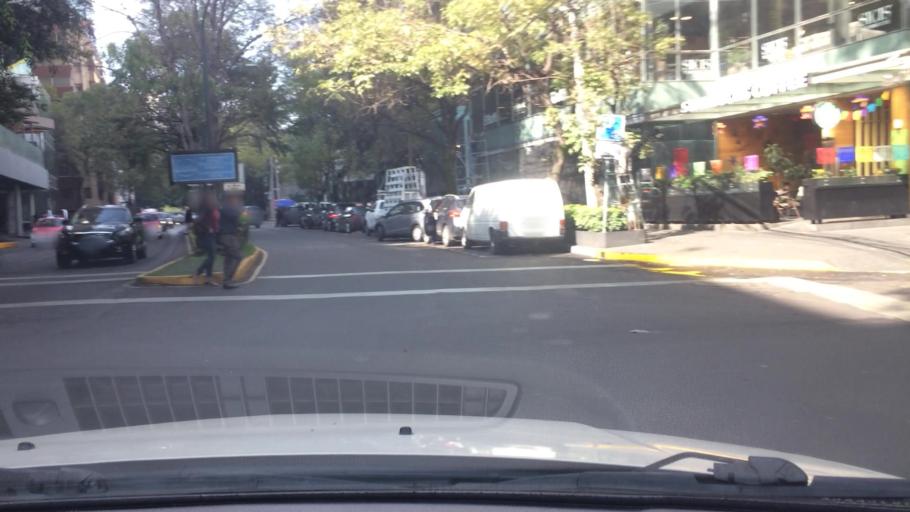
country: MX
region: Mexico City
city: Miguel Hidalgo
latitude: 19.4278
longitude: -99.1946
